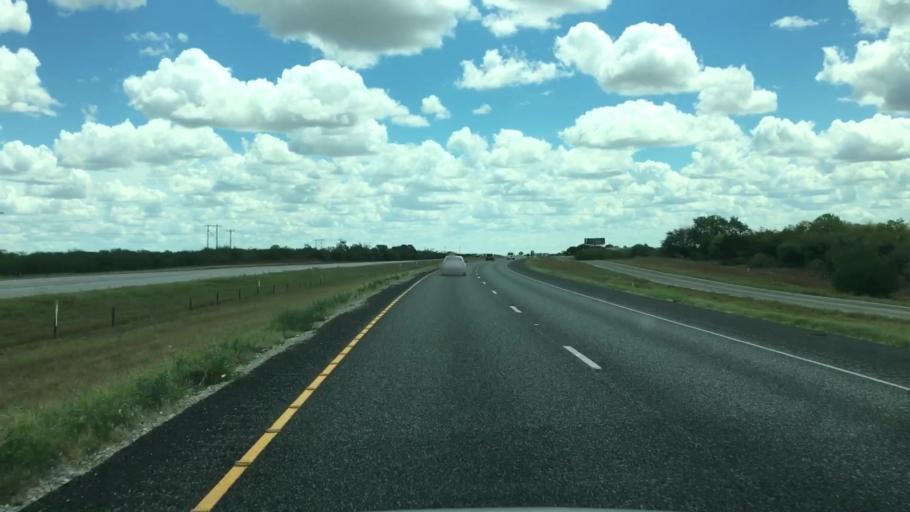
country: US
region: Texas
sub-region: Atascosa County
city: Pleasanton
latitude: 28.8857
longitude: -98.4045
